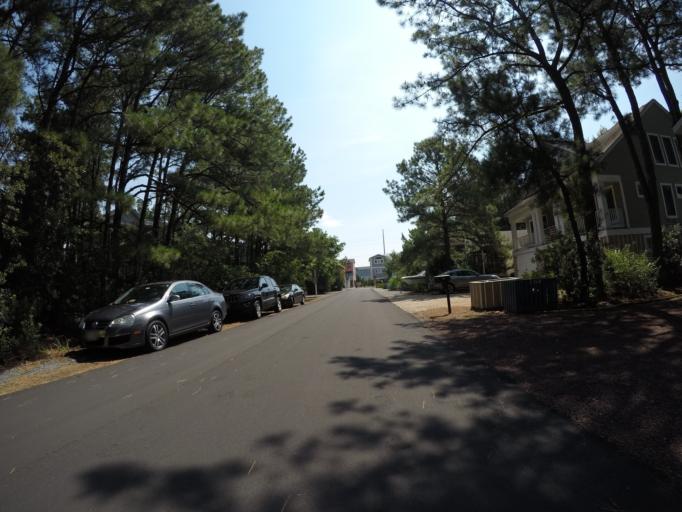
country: US
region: Delaware
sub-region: Sussex County
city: Bethany Beach
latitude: 38.5200
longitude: -75.0568
